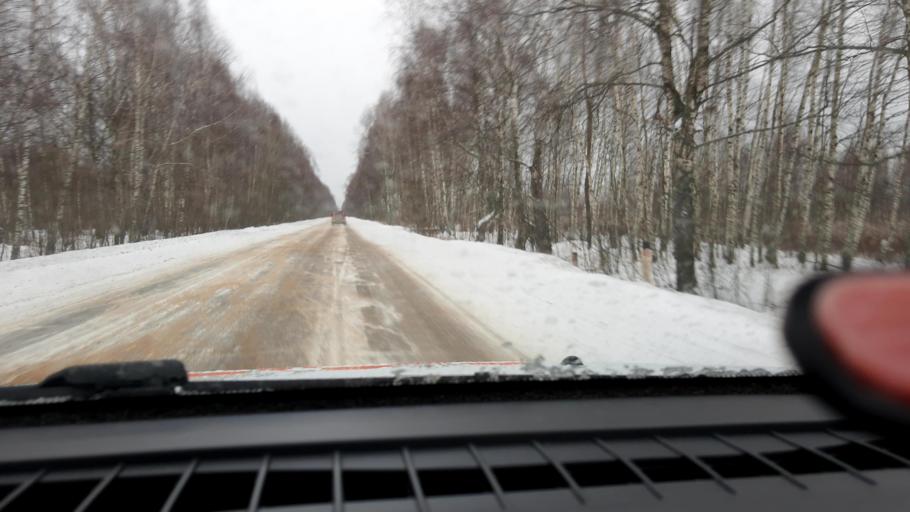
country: RU
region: Nizjnij Novgorod
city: Pamyat' Parizhskoy Kommuny
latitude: 56.2410
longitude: 44.5092
